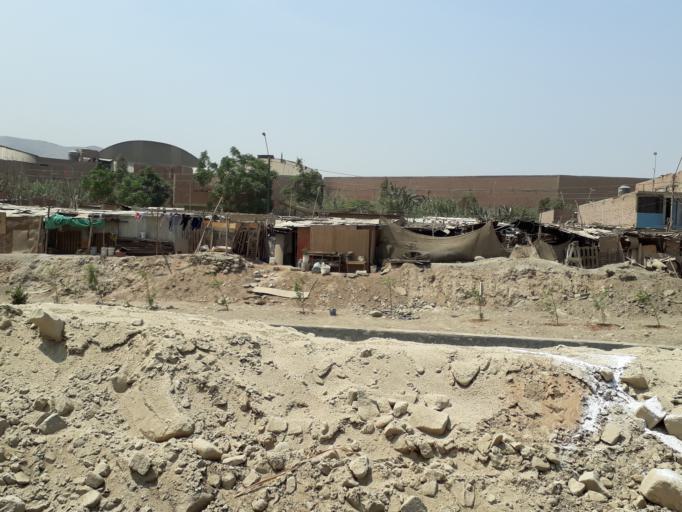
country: PE
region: Lima
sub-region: Lima
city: Santa Maria
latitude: -11.9952
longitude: -76.9104
